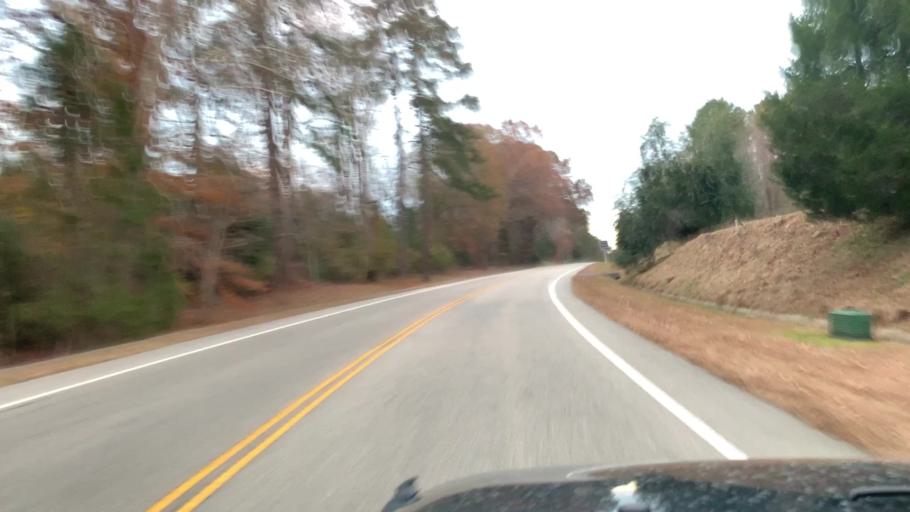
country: US
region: Virginia
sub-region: City of Williamsburg
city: Williamsburg
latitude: 37.2534
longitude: -76.7103
